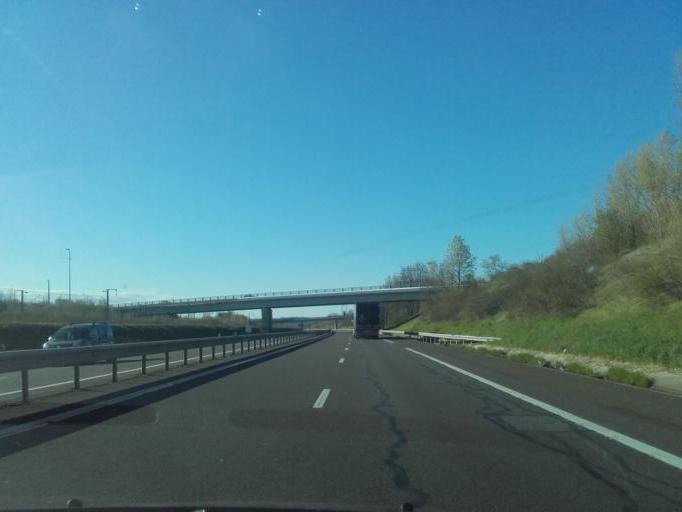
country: FR
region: Rhone-Alpes
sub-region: Departement du Rhone
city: Jons
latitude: 45.7996
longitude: 5.0735
